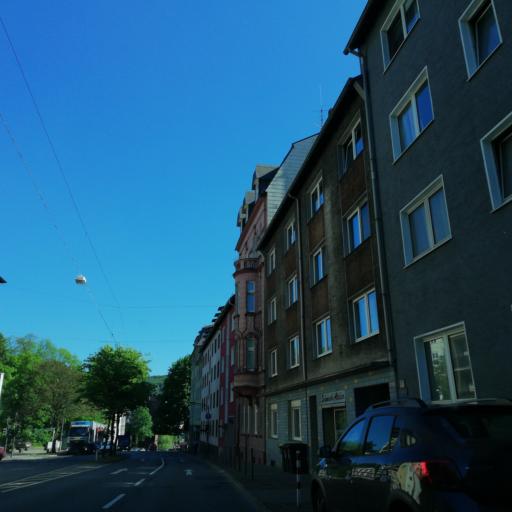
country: DE
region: North Rhine-Westphalia
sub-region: Regierungsbezirk Dusseldorf
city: Wuppertal
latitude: 51.2743
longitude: 7.1922
